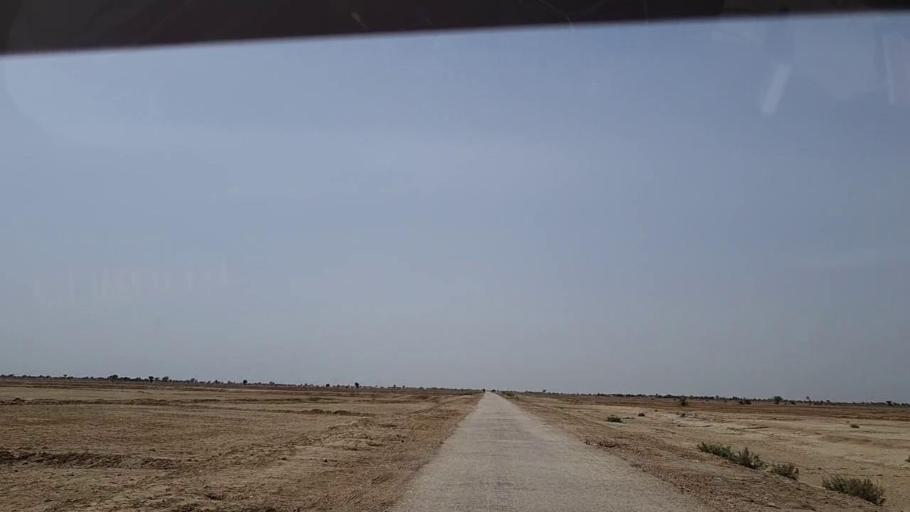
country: PK
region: Sindh
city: Johi
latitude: 26.7319
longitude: 67.6373
